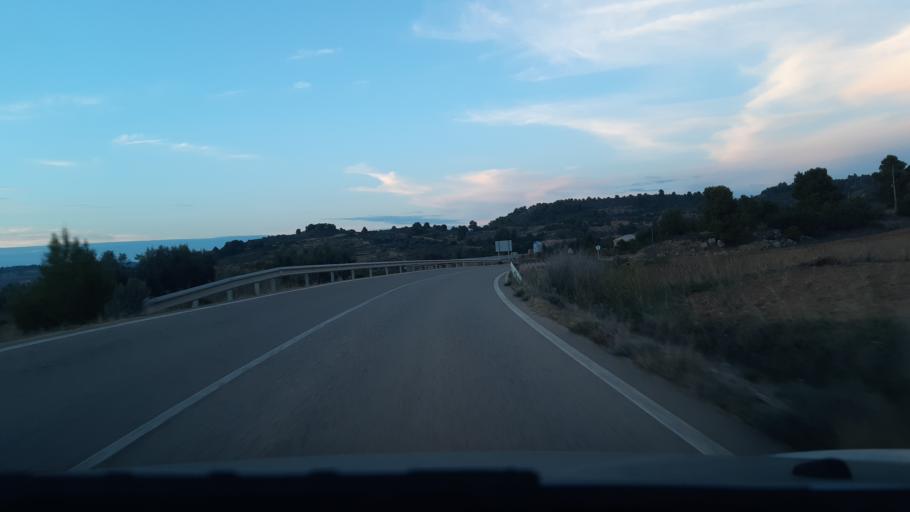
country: ES
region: Aragon
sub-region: Provincia de Teruel
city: Valderrobres
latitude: 40.8598
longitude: 0.1689
